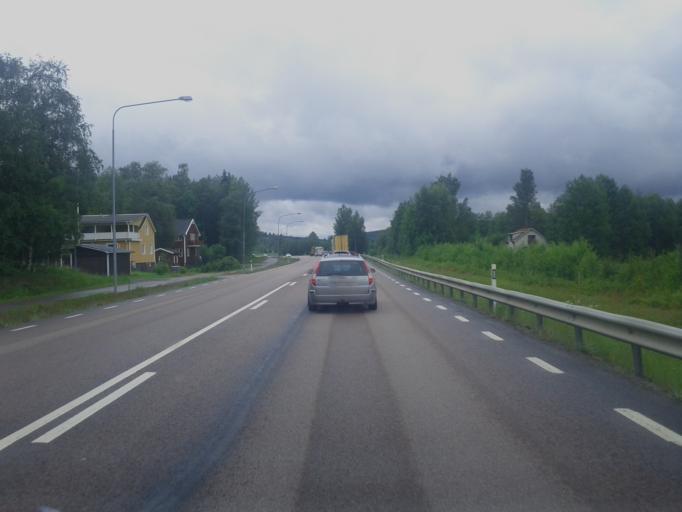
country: SE
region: Vaesternorrland
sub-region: Haernoesands Kommun
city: Haernoesand
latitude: 62.6642
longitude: 17.8524
